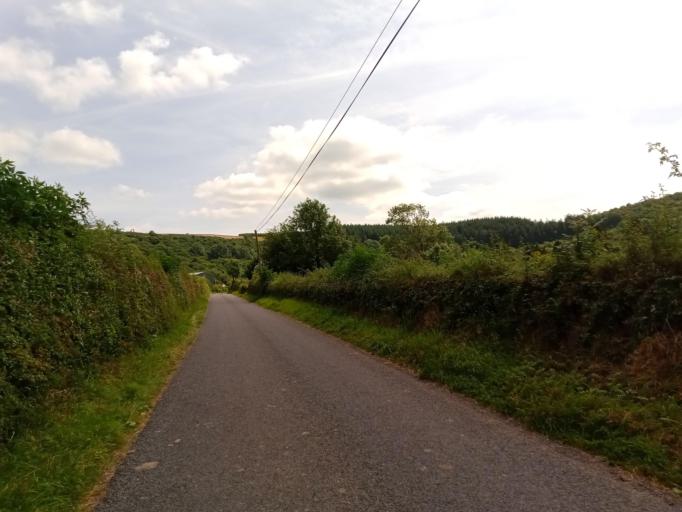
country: IE
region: Leinster
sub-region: Laois
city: Rathdowney
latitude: 52.8066
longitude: -7.4654
